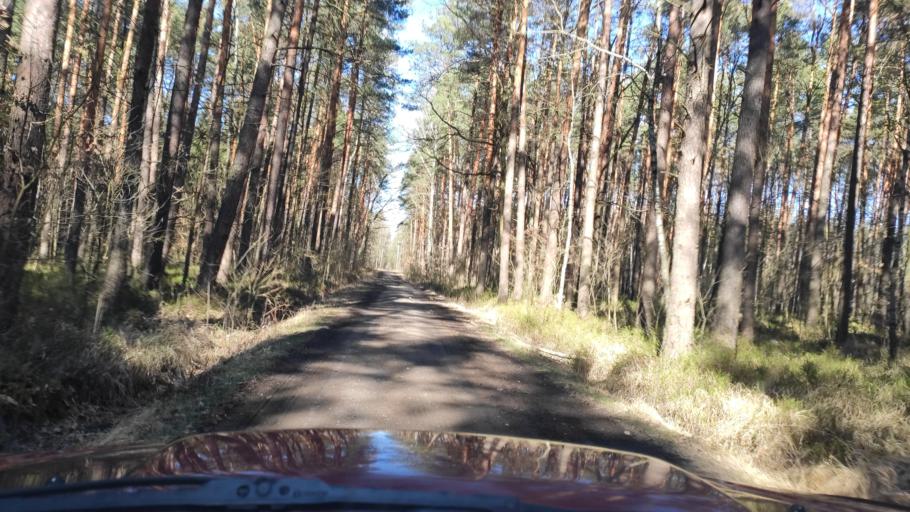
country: PL
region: Masovian Voivodeship
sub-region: Powiat kozienicki
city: Garbatka-Letnisko
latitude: 51.4390
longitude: 21.5432
